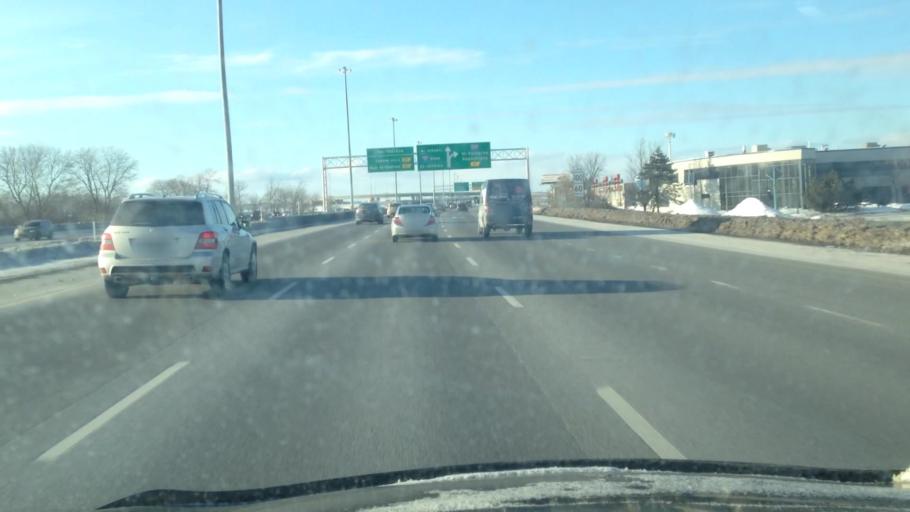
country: CA
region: Quebec
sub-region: Laurentides
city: Boisbriand
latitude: 45.6214
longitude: -73.8313
